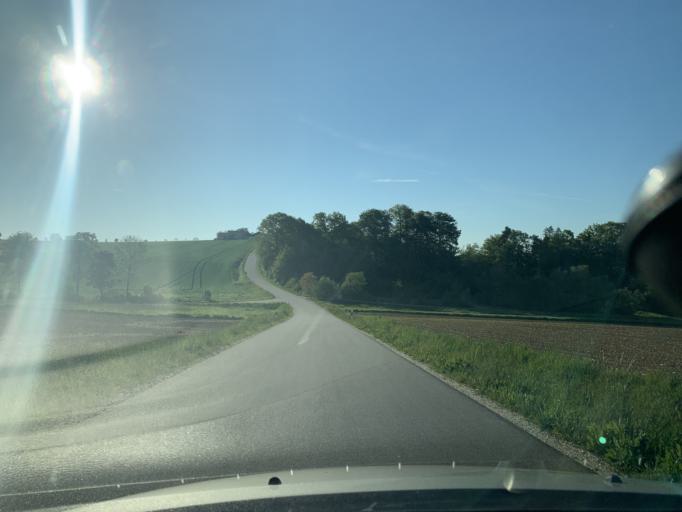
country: DE
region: Bavaria
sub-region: Lower Bavaria
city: Adlkofen
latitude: 48.5203
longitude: 12.3128
